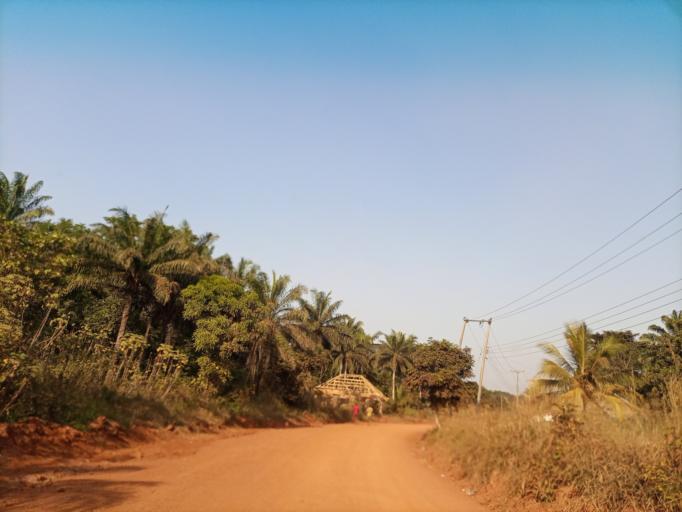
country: NG
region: Enugu
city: Opi
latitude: 6.7767
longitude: 7.3859
